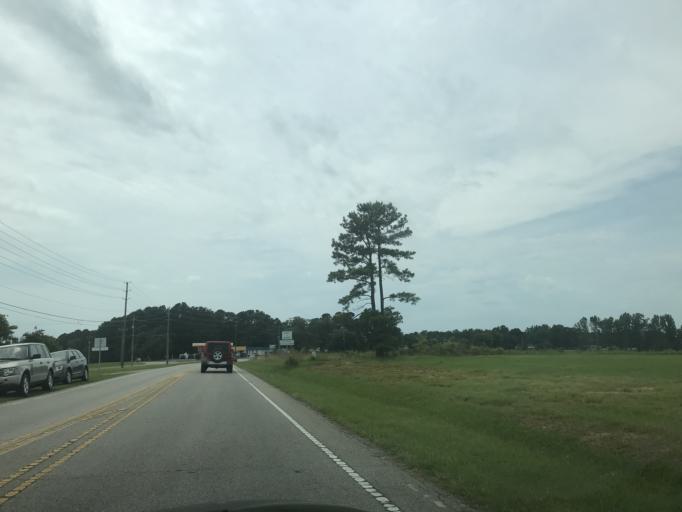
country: US
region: North Carolina
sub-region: Vance County
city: Henderson
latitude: 36.3382
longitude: -78.4431
